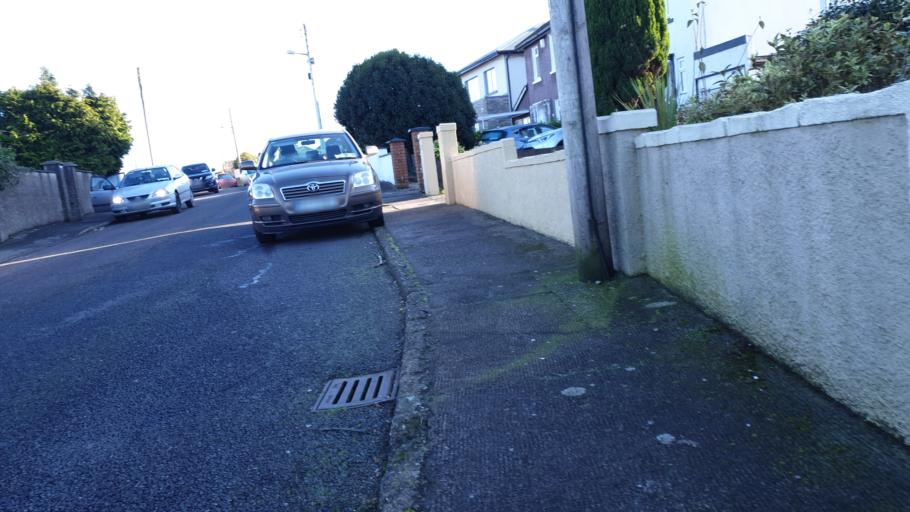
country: IE
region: Munster
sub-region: County Cork
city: Cork
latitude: 51.8924
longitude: -8.4273
